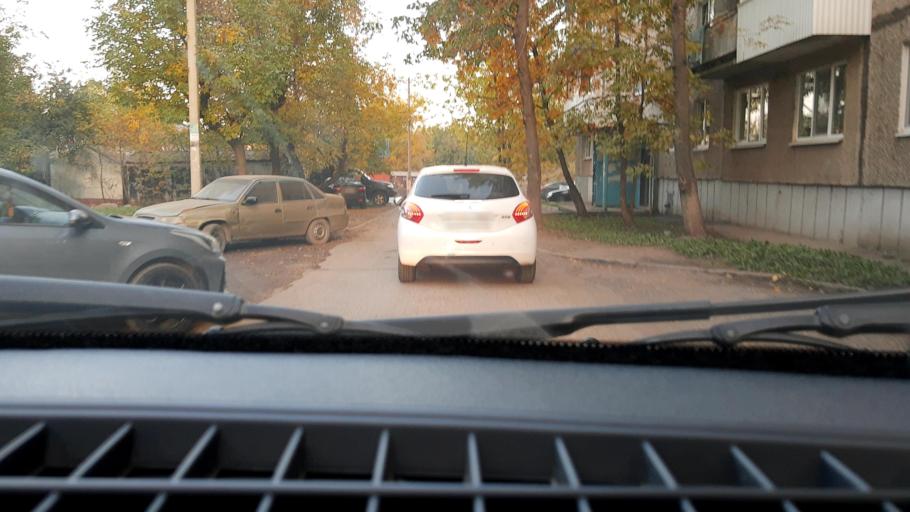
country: RU
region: Bashkortostan
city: Ufa
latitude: 54.7406
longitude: 56.0013
